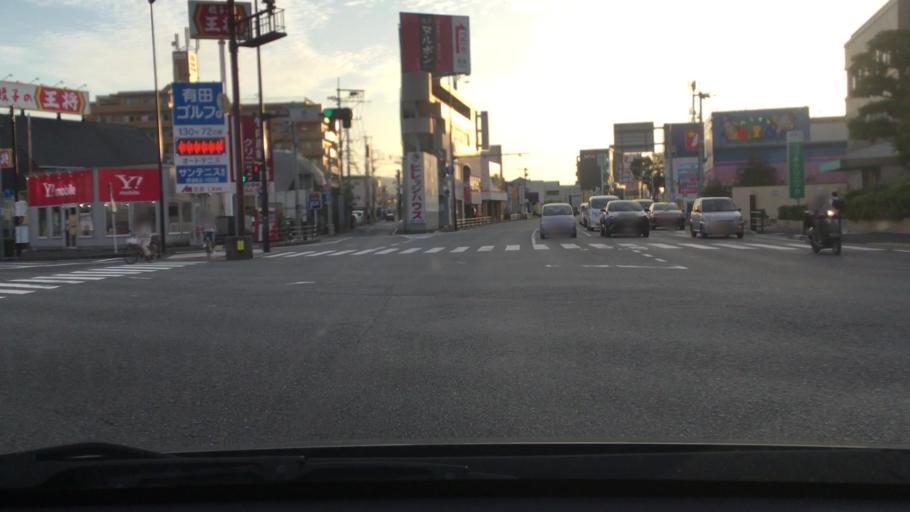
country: JP
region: Fukuoka
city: Fukuoka-shi
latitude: 33.5670
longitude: 130.3431
